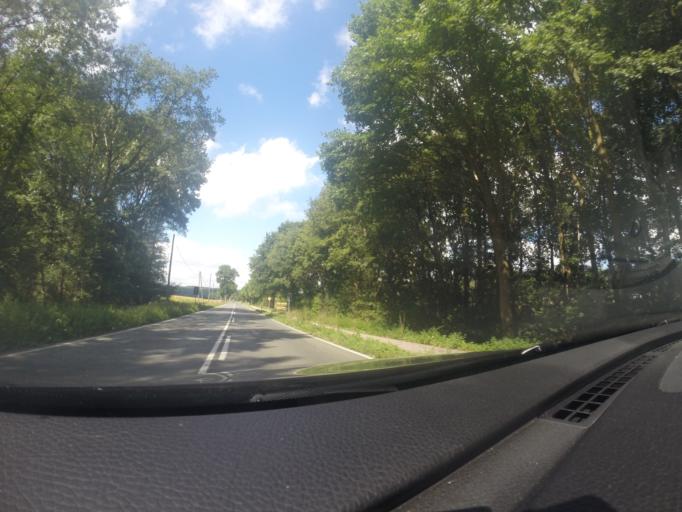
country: DE
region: North Rhine-Westphalia
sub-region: Regierungsbezirk Dusseldorf
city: Emmerich
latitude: 51.8540
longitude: 6.1977
